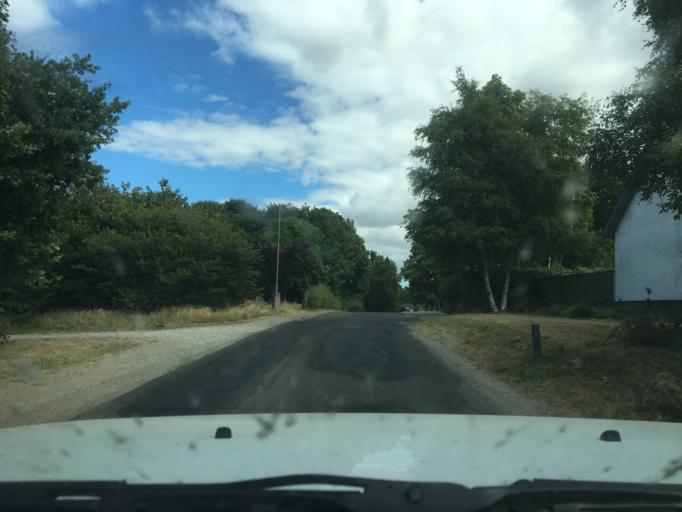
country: DK
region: Central Jutland
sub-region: Syddjurs Kommune
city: Ryomgard
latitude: 56.4623
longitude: 10.6305
